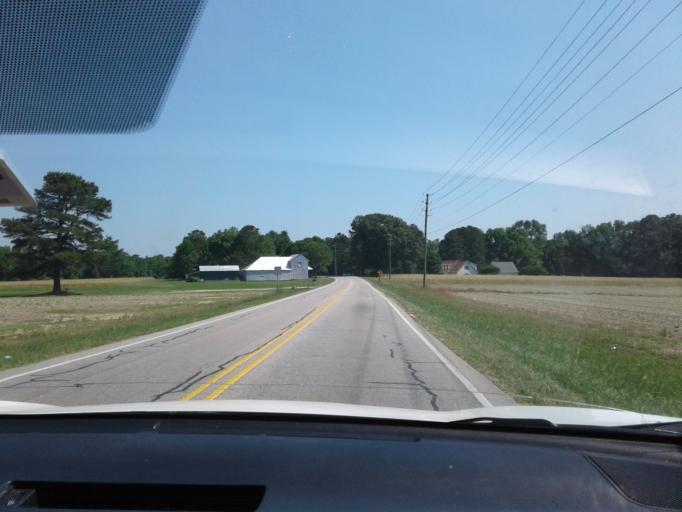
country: US
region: North Carolina
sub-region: Wake County
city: Fuquay-Varina
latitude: 35.5878
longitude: -78.8393
